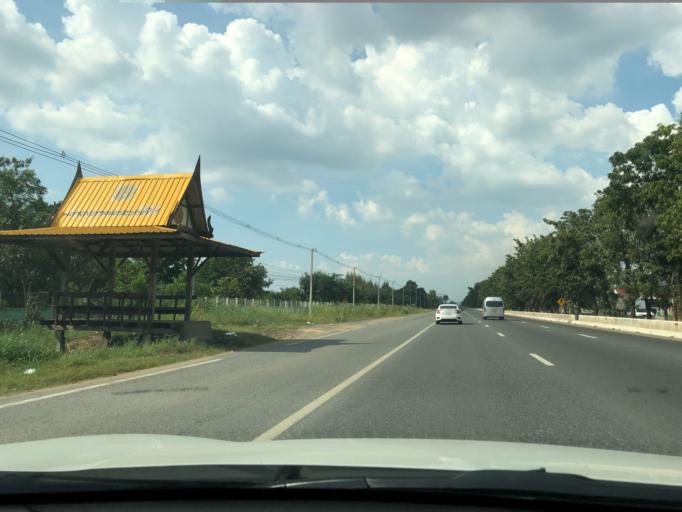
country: TH
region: Nakhon Sawan
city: Krok Phra
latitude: 15.5795
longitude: 100.1246
